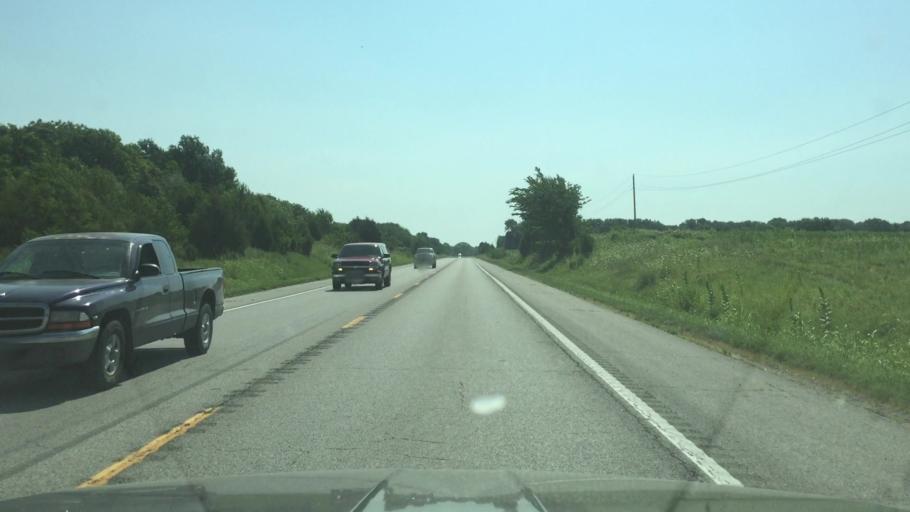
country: US
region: Missouri
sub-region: Pettis County
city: Sedalia
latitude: 38.6933
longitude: -93.0858
